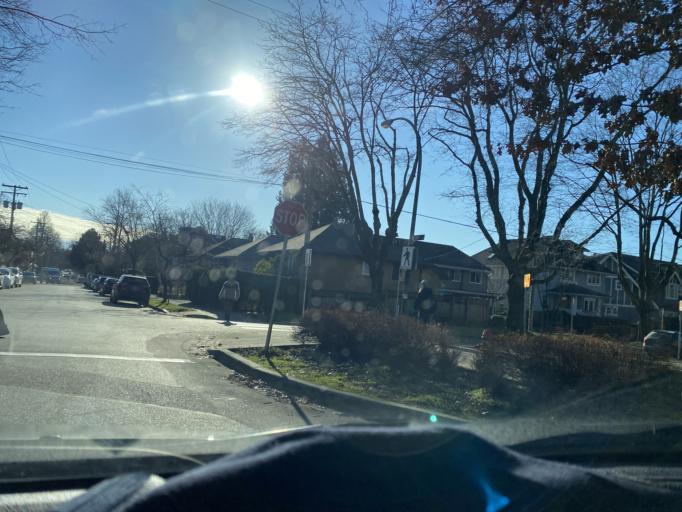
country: CA
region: British Columbia
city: West End
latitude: 49.2659
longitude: -123.1576
